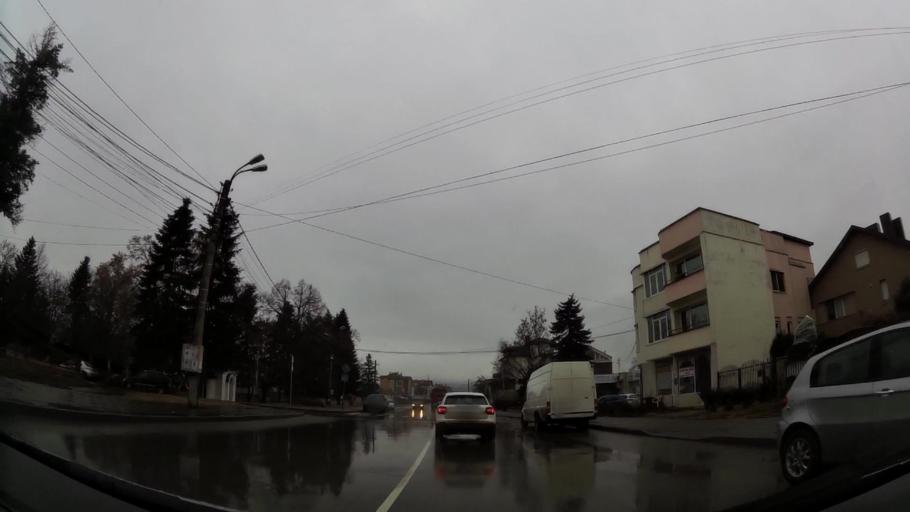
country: BG
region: Sofia-Capital
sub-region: Stolichna Obshtina
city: Sofia
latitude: 42.6266
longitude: 23.4068
